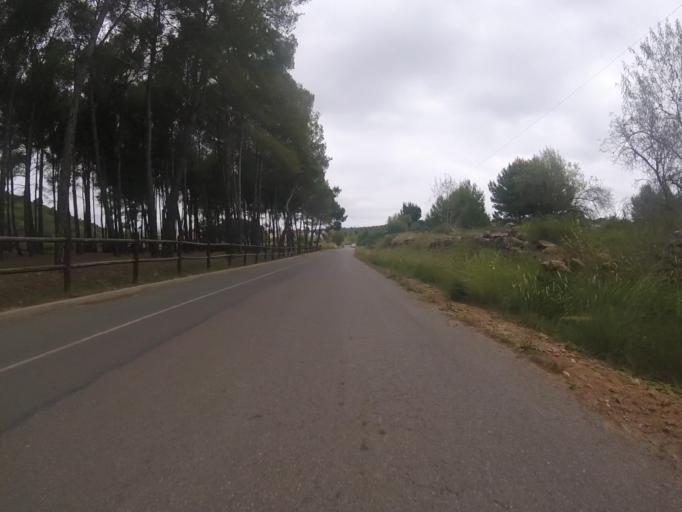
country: ES
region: Valencia
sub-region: Provincia de Castello
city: Cabanes
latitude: 40.1498
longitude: 0.0469
